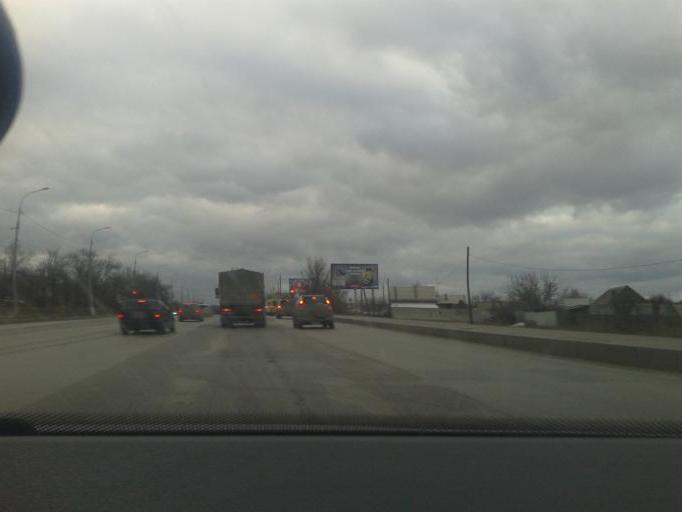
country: RU
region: Volgograd
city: Volgograd
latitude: 48.6697
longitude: 44.4420
